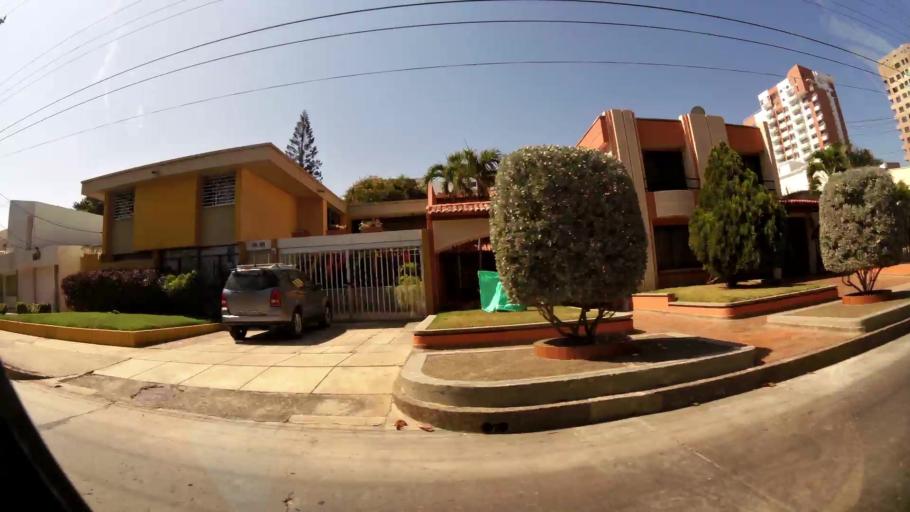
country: CO
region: Atlantico
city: Barranquilla
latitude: 11.0141
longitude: -74.8164
